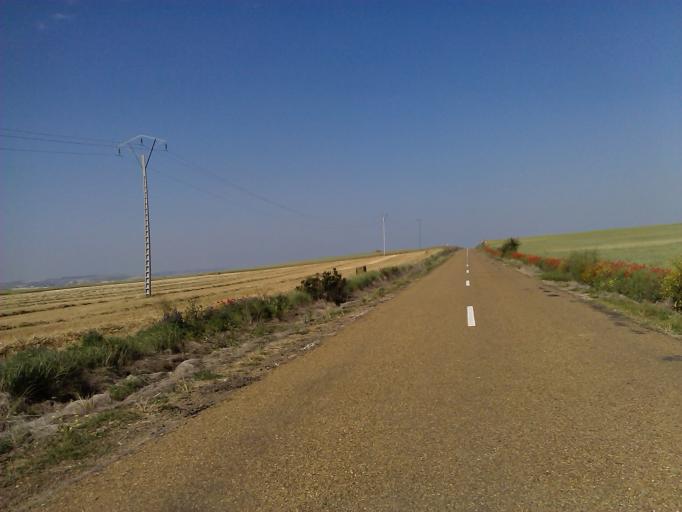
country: ES
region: Castille and Leon
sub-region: Provincia de Palencia
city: Melgar de Yuso
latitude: 42.2618
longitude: -4.2889
